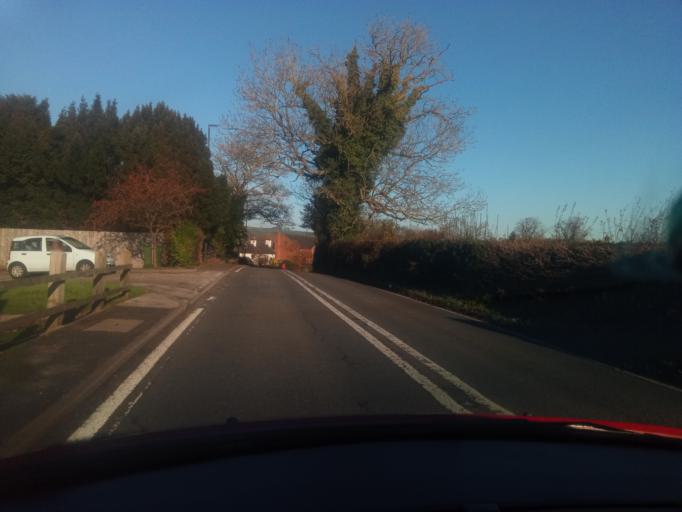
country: GB
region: England
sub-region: Derbyshire
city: Wirksworth
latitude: 53.0144
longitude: -1.5625
